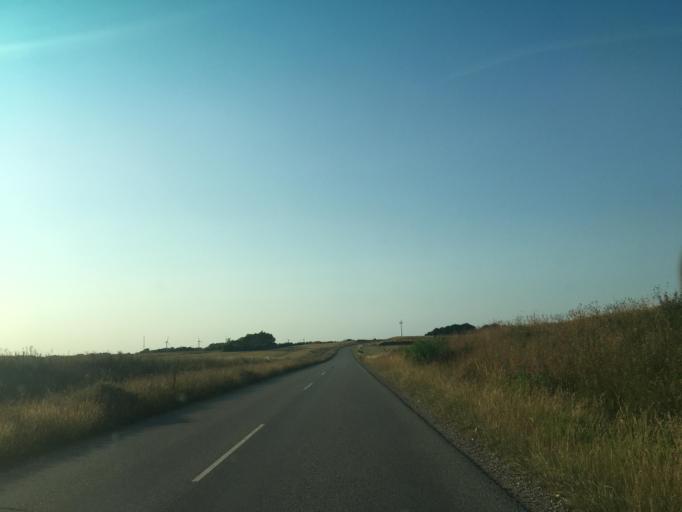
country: DK
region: North Denmark
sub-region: Thisted Kommune
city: Hurup
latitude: 56.7622
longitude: 8.4233
